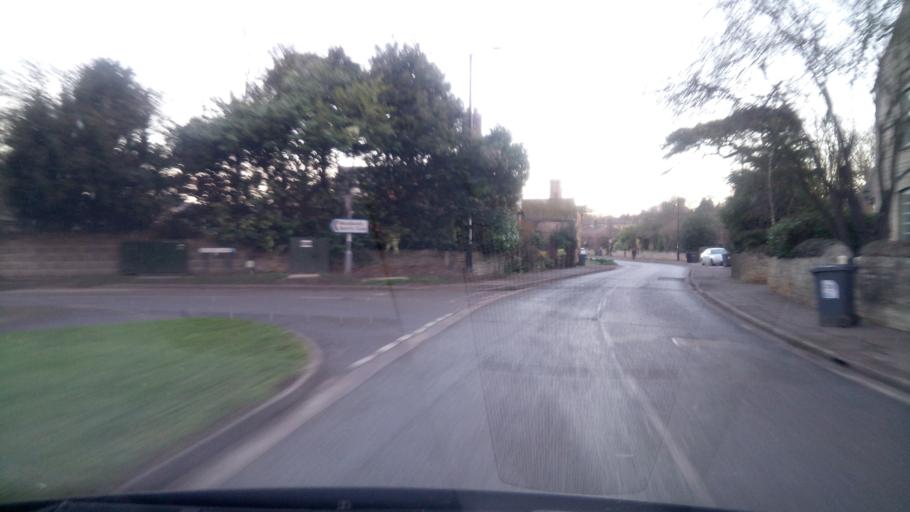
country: GB
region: England
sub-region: Peterborough
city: Castor
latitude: 52.5705
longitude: -0.3405
